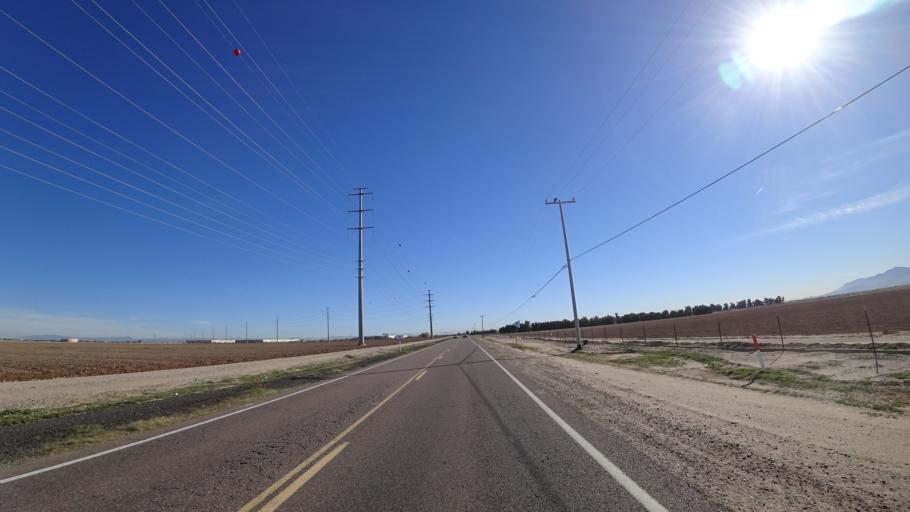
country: US
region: Arizona
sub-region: Maricopa County
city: Citrus Park
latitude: 33.4939
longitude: -112.4413
